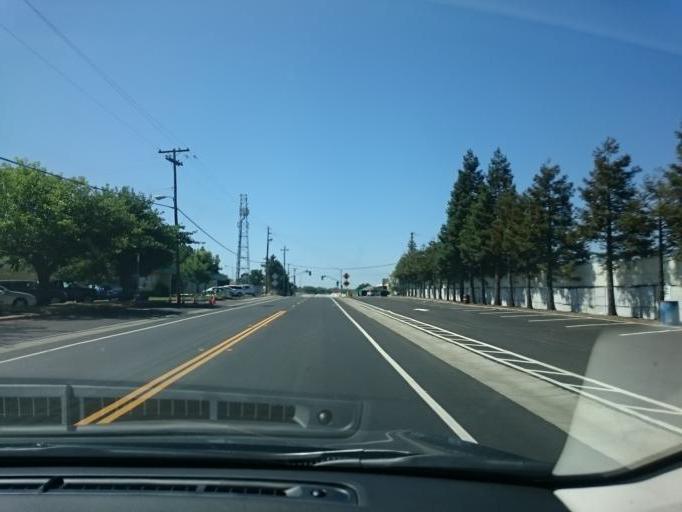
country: US
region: California
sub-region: Yolo County
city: West Sacramento
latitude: 38.5640
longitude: -121.5235
